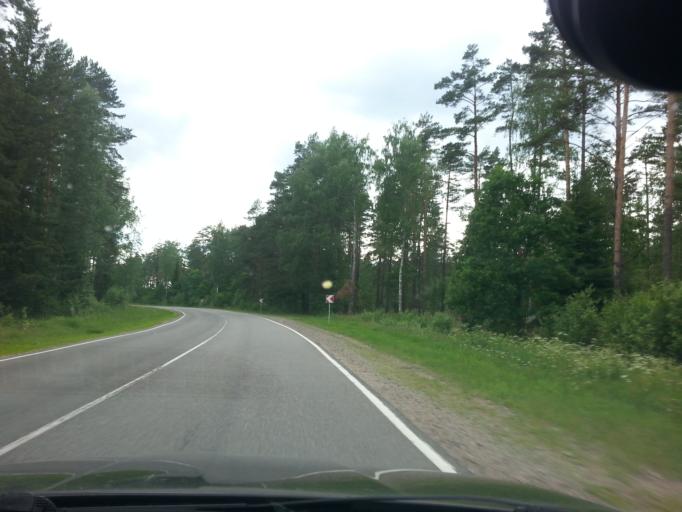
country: BY
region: Minsk
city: Svir
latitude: 54.8499
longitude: 26.2540
